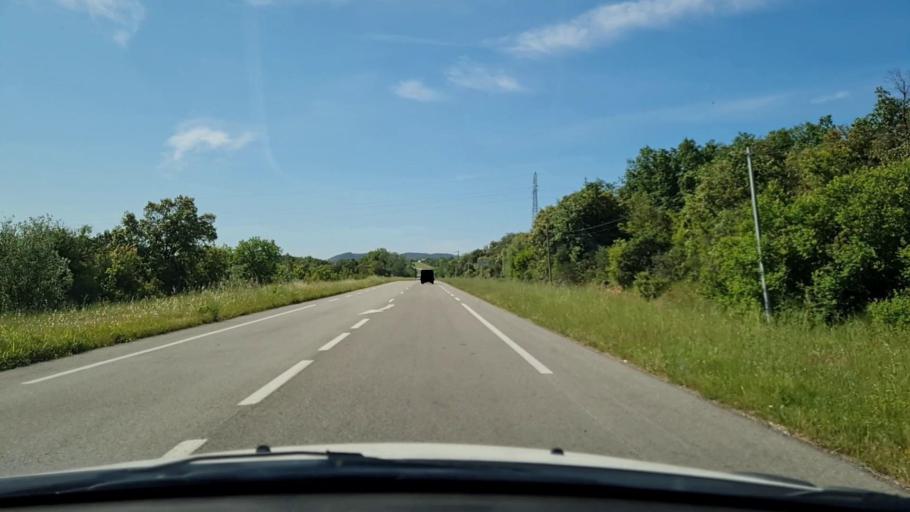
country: FR
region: Languedoc-Roussillon
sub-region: Departement du Gard
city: Vezenobres
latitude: 44.0401
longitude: 4.1471
